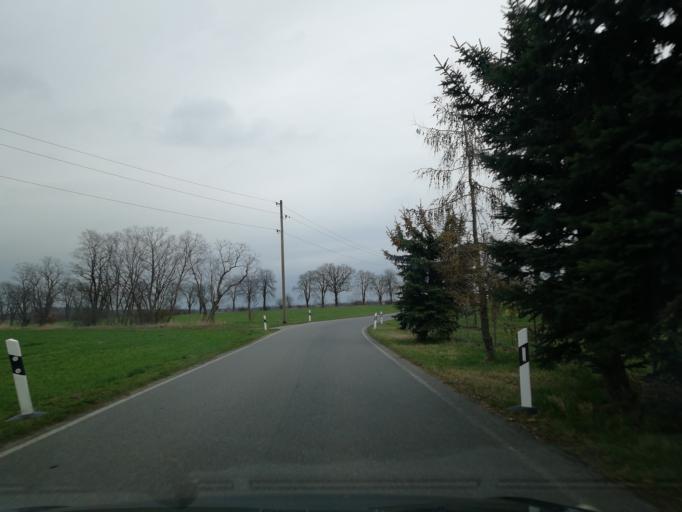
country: DE
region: Brandenburg
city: Calau
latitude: 51.7298
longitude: 14.0245
